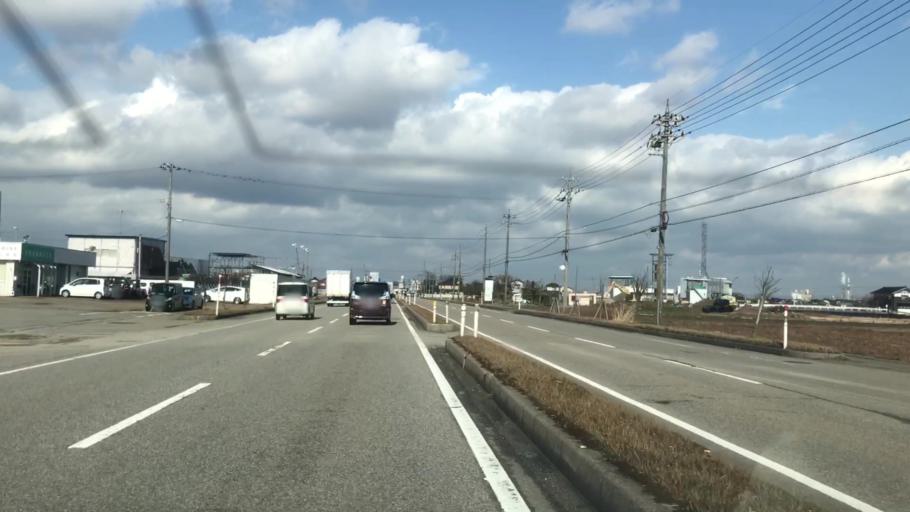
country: JP
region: Toyama
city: Kuragaki-kosugi
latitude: 36.7122
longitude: 137.0809
